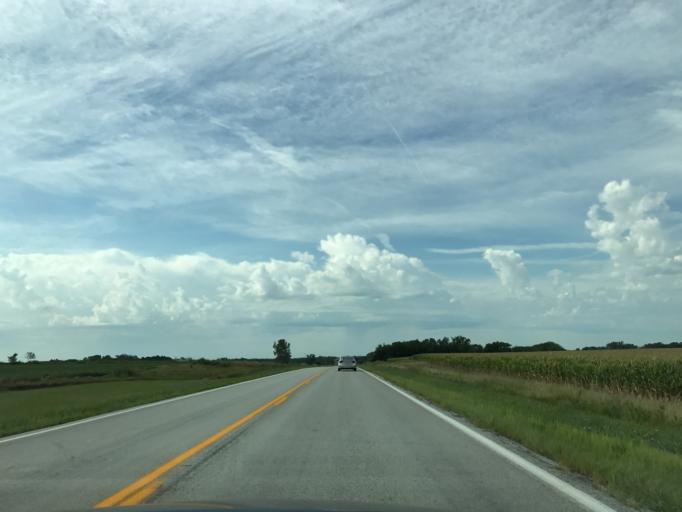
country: US
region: Nebraska
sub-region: Saline County
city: Friend
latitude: 40.5171
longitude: -97.1793
